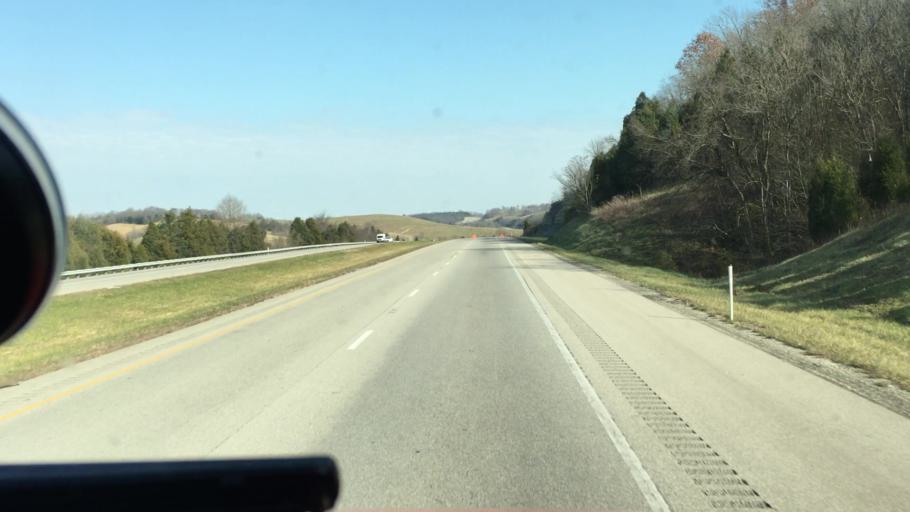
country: US
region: Kentucky
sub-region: Bath County
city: Owingsville
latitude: 38.1078
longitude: -83.8198
